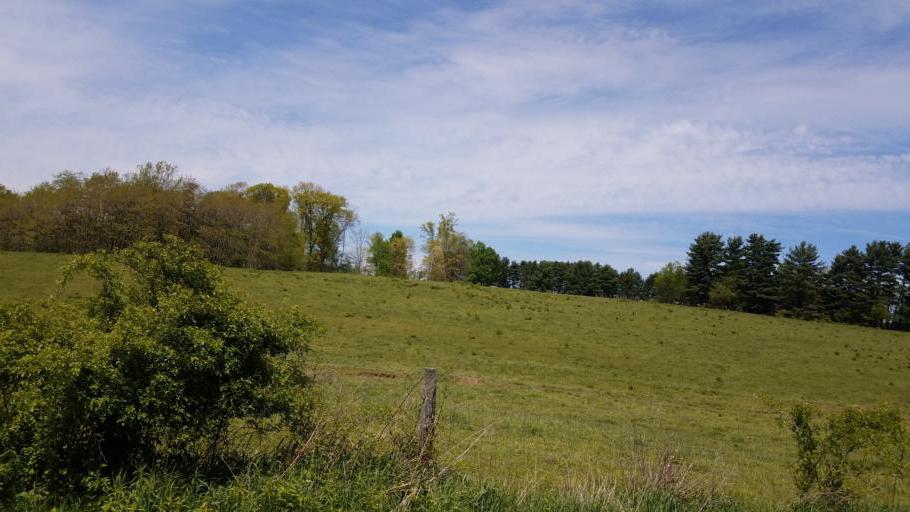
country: US
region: Ohio
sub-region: Knox County
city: Gambier
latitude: 40.4234
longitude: -82.3701
